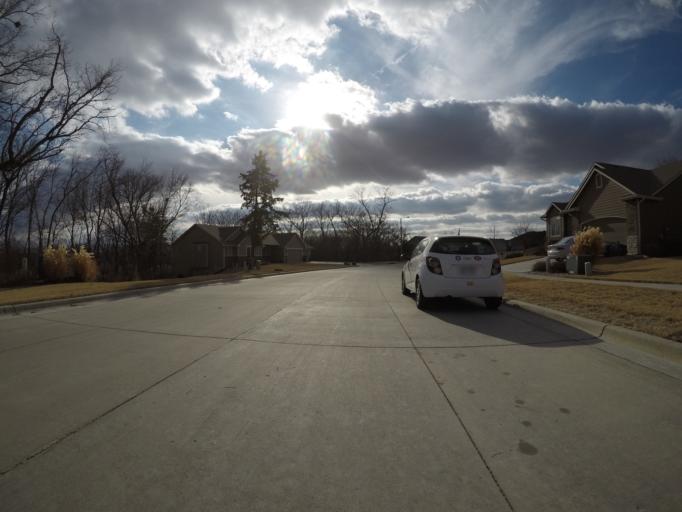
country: US
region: Kansas
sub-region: Riley County
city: Manhattan
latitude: 39.1646
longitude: -96.6389
